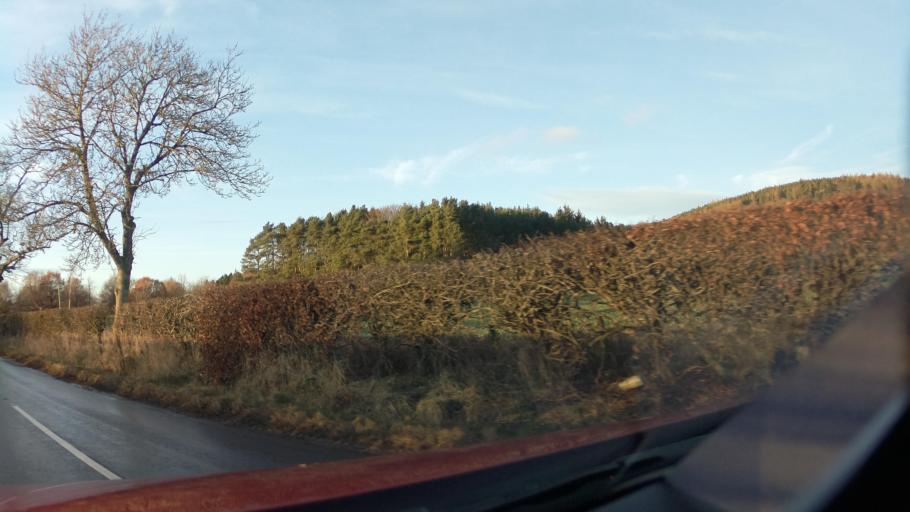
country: GB
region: Scotland
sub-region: Angus
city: Forfar
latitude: 56.5875
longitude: -2.8735
